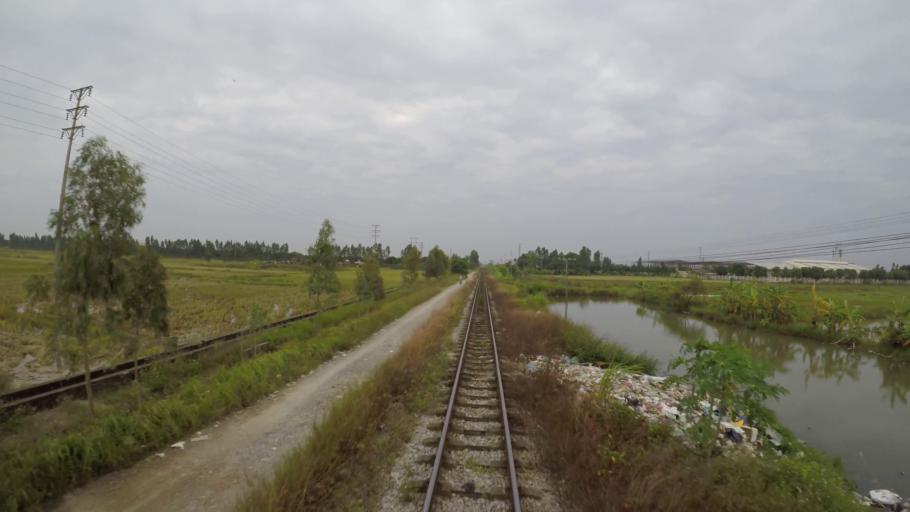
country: VN
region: Hai Duong
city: Lai Cach
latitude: 20.9477
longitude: 106.2580
